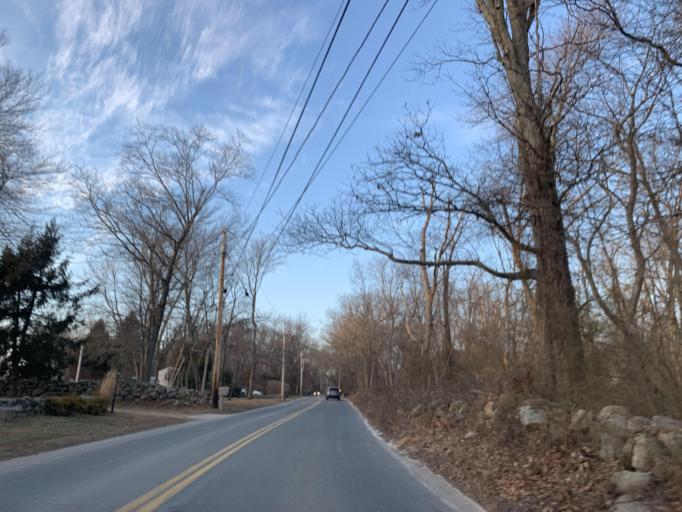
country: US
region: Rhode Island
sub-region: Washington County
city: Kingston
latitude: 41.4793
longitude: -71.4986
